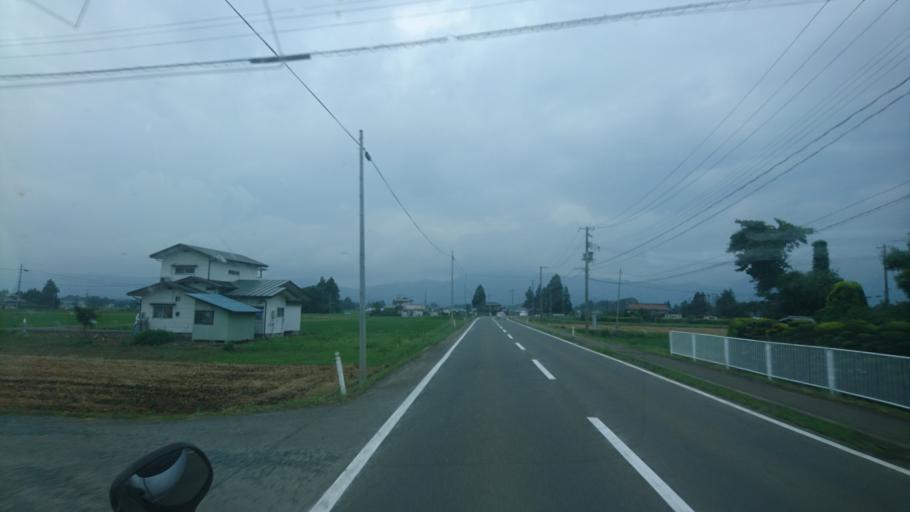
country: JP
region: Iwate
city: Morioka-shi
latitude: 39.5915
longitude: 141.1674
